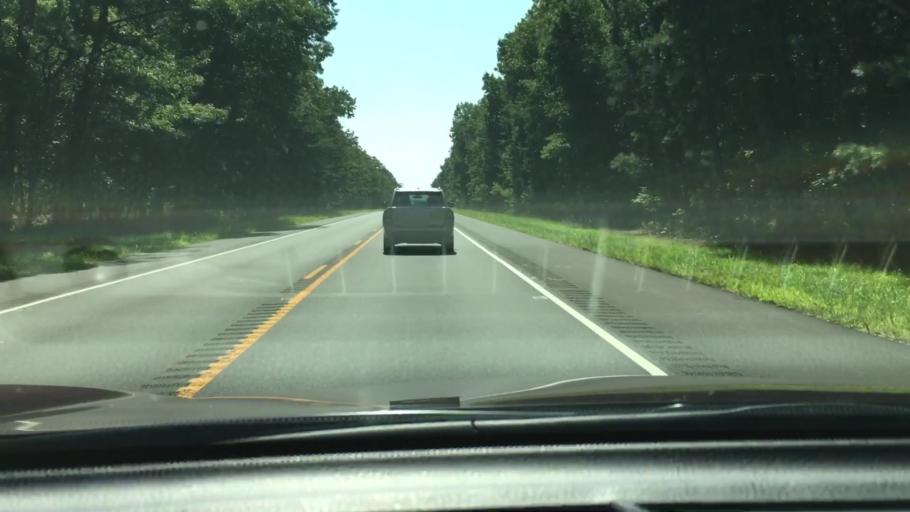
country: US
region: New Jersey
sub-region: Cape May County
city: Woodbine
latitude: 39.3311
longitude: -74.8766
